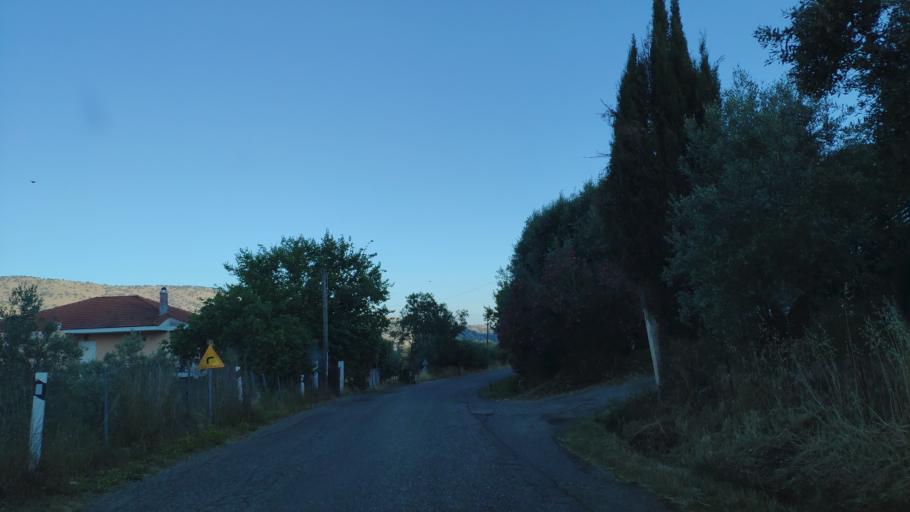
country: GR
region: West Greece
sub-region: Nomos Aitolias kai Akarnanias
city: Astakos
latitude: 38.5703
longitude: 21.0948
